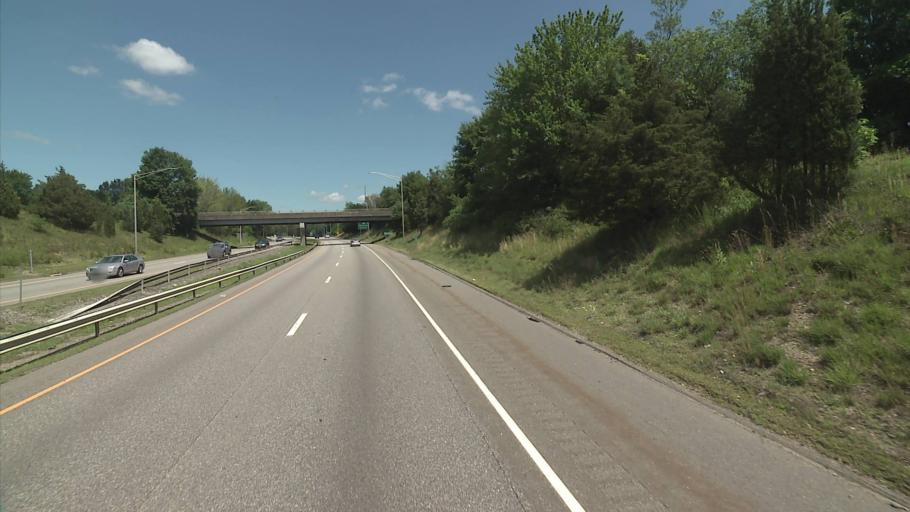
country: US
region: Connecticut
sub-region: New London County
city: Norwich
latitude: 41.5044
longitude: -72.1146
